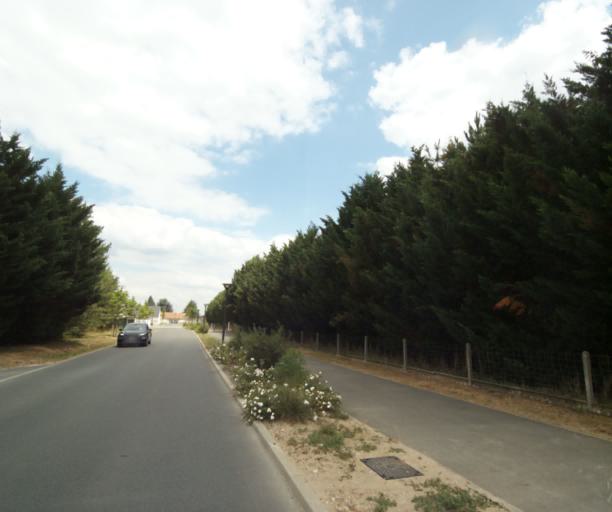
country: FR
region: Centre
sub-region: Departement du Loiret
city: Saint-Pryve-Saint-Mesmin
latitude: 47.8610
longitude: 1.8746
